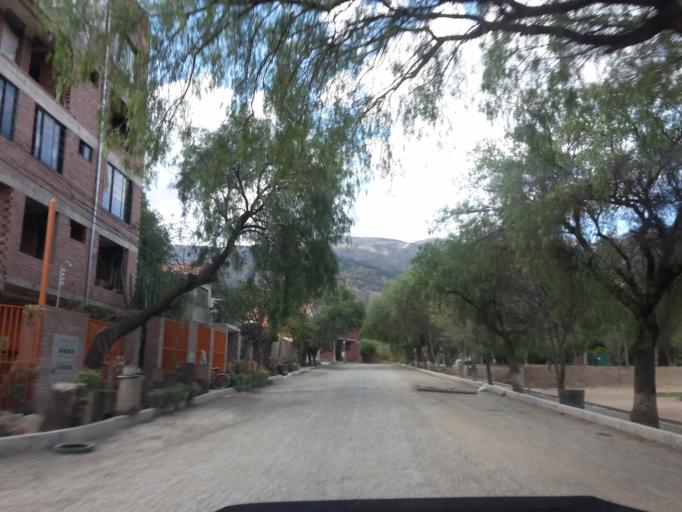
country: BO
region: Cochabamba
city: Cochabamba
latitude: -17.3373
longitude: -66.2144
